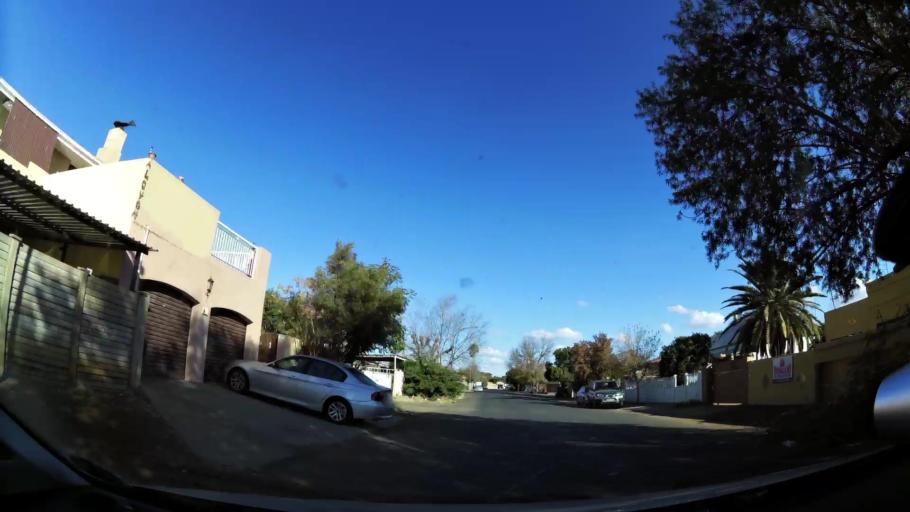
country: ZA
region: Northern Cape
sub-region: Frances Baard District Municipality
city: Kimberley
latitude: -28.7477
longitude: 24.7617
